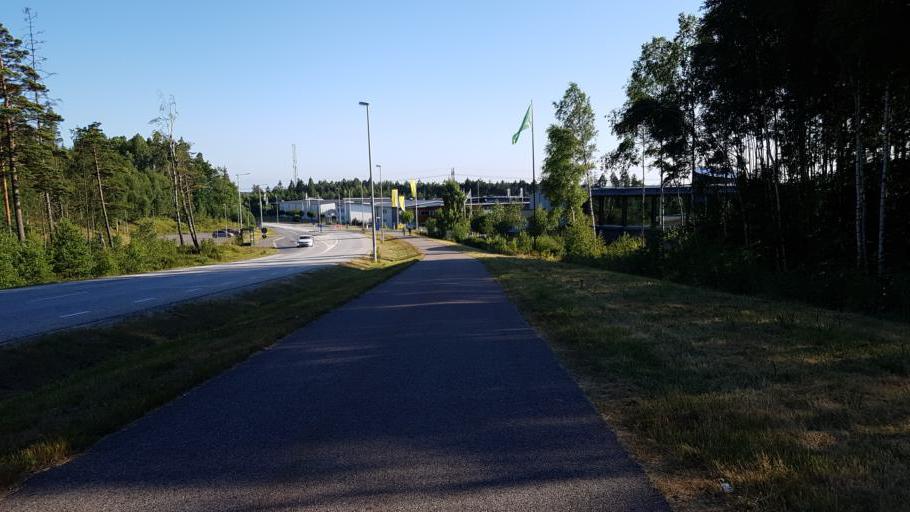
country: SE
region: Vaestra Goetaland
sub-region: Partille Kommun
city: Ojersjo
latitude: 57.6810
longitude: 12.0951
